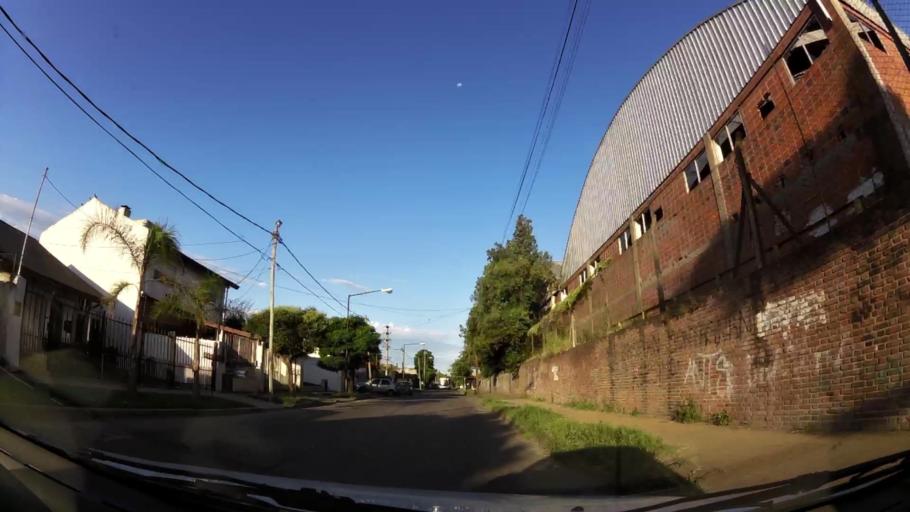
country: AR
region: Buenos Aires
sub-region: Partido de San Isidro
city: San Isidro
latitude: -34.4696
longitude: -58.5503
